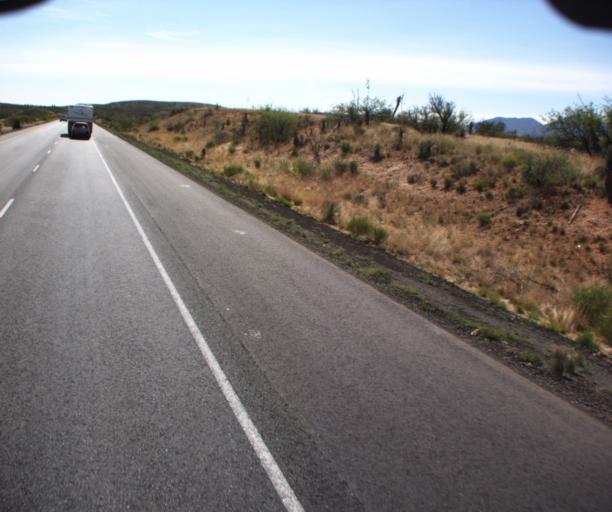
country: US
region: Arizona
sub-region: Cochise County
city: Mescal
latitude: 31.9713
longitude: -110.4892
